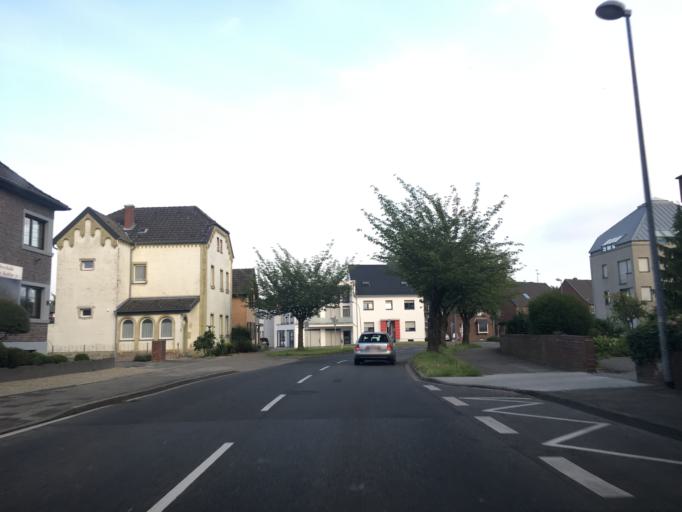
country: DE
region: North Rhine-Westphalia
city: Huckelhoven
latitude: 51.0502
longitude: 6.2281
